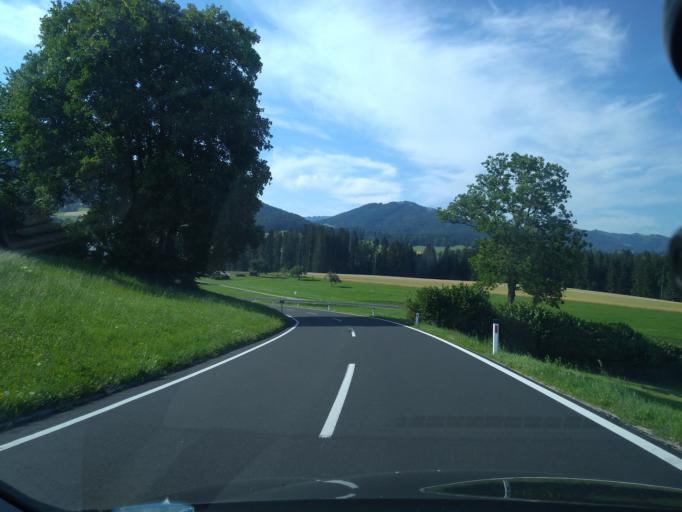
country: AT
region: Styria
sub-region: Politischer Bezirk Graz-Umgebung
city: Semriach
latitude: 47.2675
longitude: 15.4436
